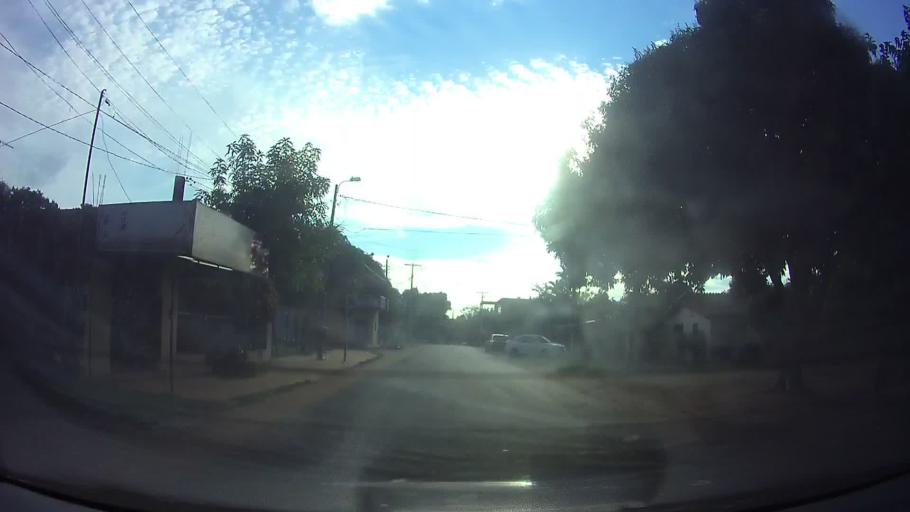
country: PY
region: Central
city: San Lorenzo
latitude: -25.2777
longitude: -57.4836
